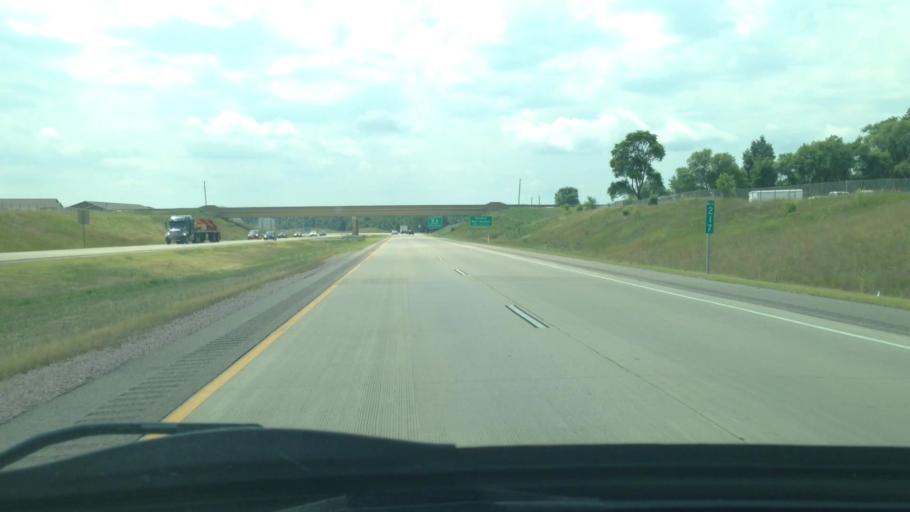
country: US
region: Wisconsin
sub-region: Sauk County
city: West Baraboo
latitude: 43.4986
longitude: -89.7819
